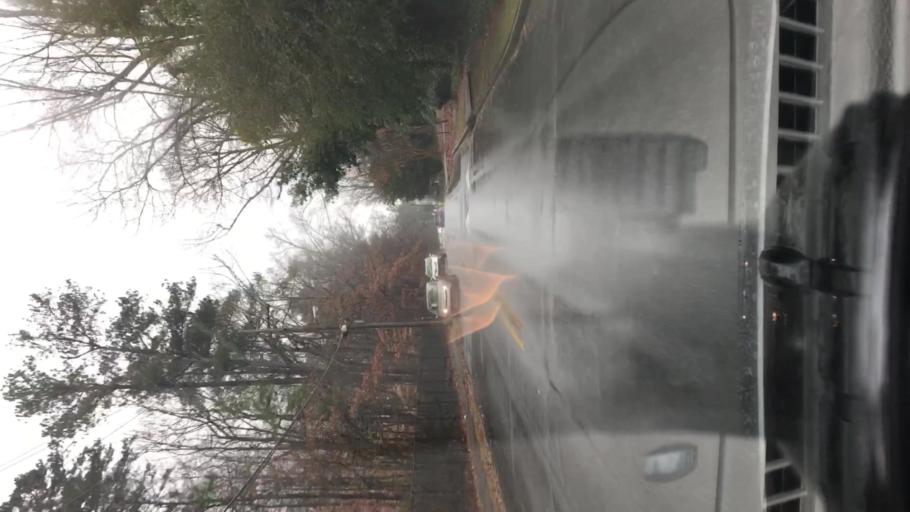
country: US
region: Georgia
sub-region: DeKalb County
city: North Atlanta
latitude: 33.8786
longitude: -84.3380
